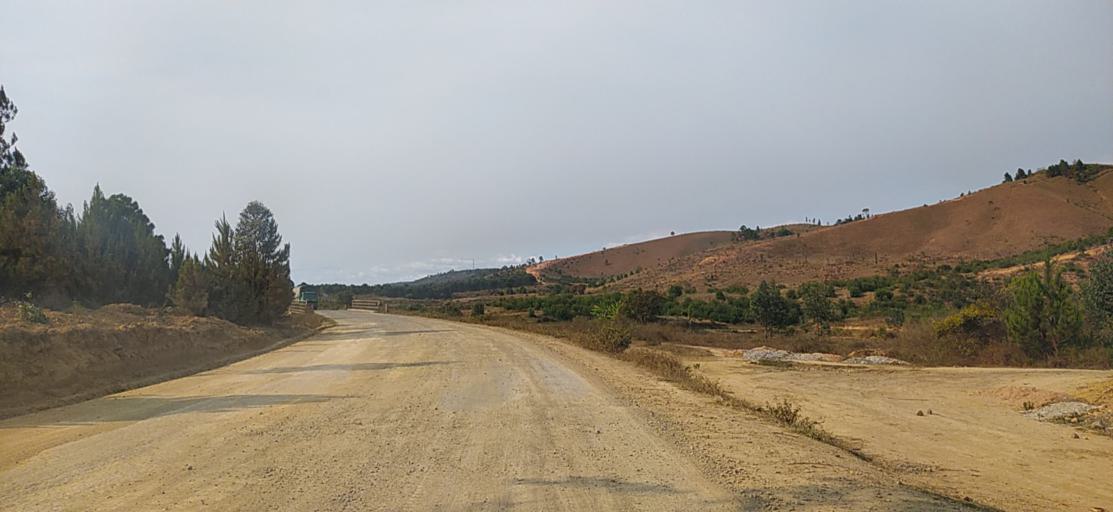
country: MG
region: Alaotra Mangoro
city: Moramanga
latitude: -18.6673
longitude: 48.2745
